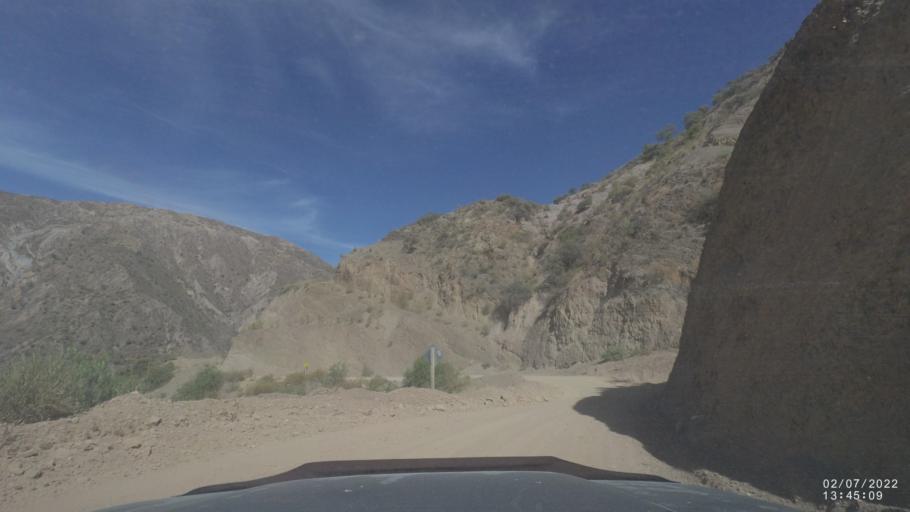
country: BO
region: Cochabamba
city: Irpa Irpa
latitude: -17.8072
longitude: -66.3656
